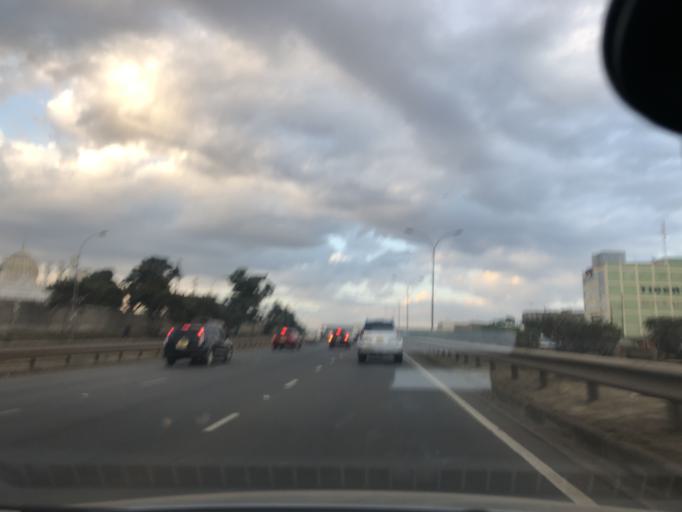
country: KE
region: Kiambu
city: Kiambu
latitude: -1.1987
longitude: 36.9215
